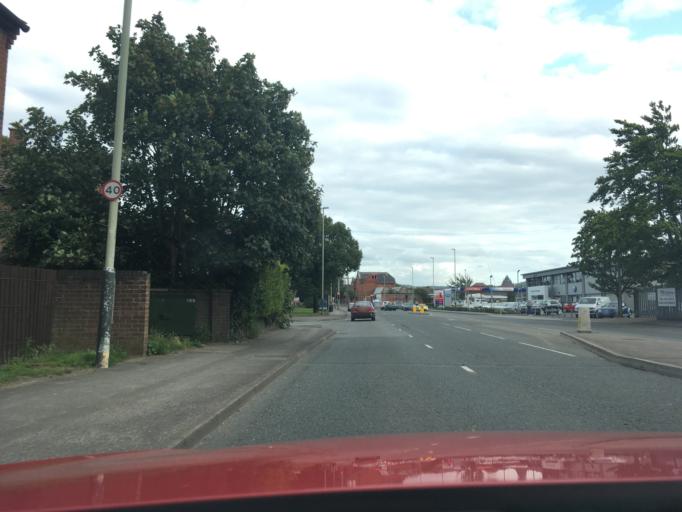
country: GB
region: England
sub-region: Gloucestershire
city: Cheltenham
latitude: 51.9083
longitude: -2.0892
